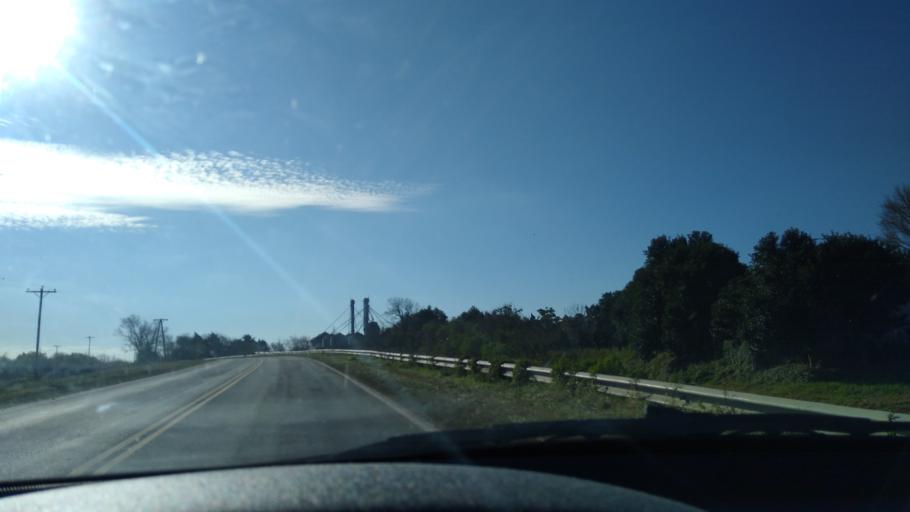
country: AR
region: Entre Rios
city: Aranguren
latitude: -32.3653
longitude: -60.3453
